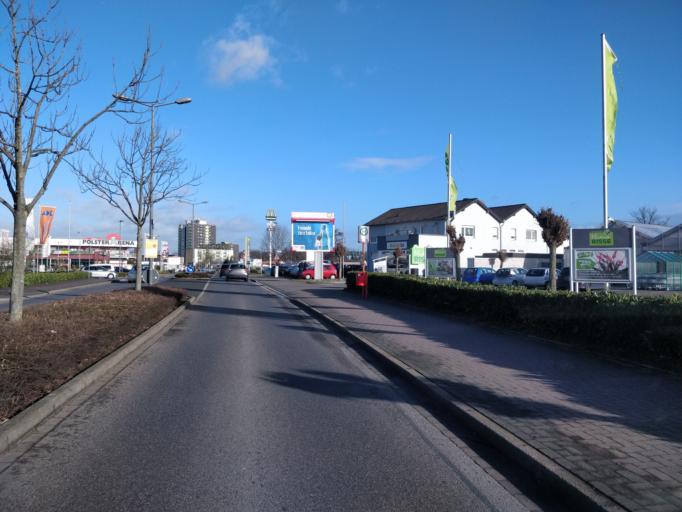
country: DE
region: North Rhine-Westphalia
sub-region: Regierungsbezirk Dusseldorf
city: Dormagen
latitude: 51.0921
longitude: 6.8135
